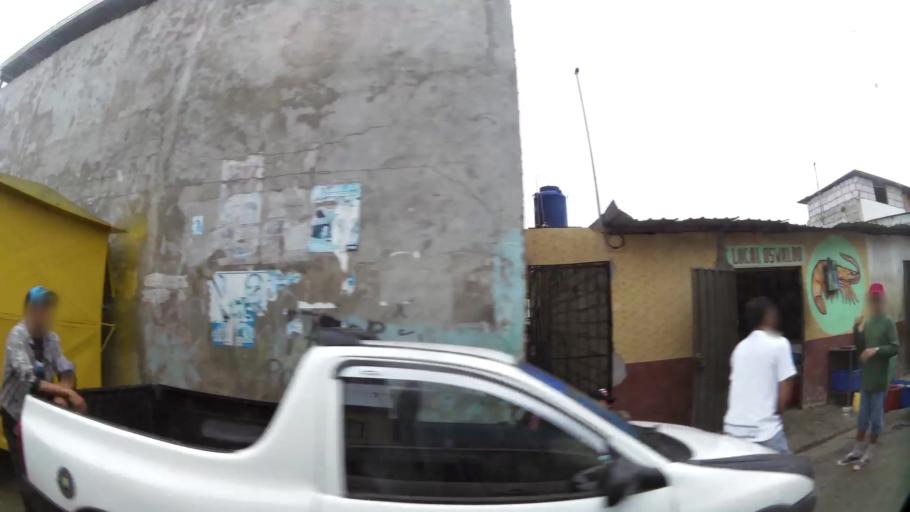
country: EC
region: El Oro
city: Puerto Bolivar
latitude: -3.2724
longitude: -80.0018
